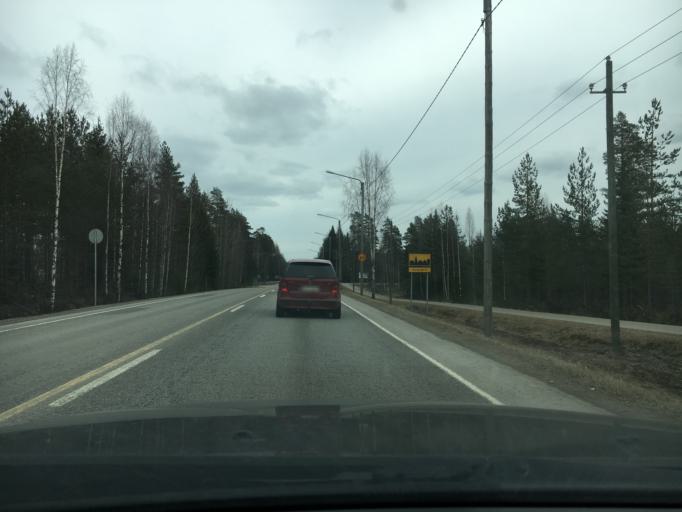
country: FI
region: Central Finland
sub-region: AEaenekoski
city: Suolahti
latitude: 62.5632
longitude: 25.8158
